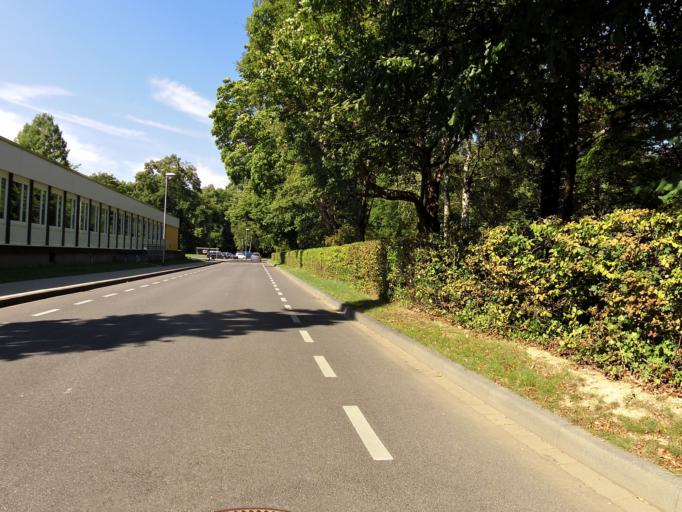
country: DE
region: North Rhine-Westphalia
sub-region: Regierungsbezirk Koln
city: Rheinbach
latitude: 50.6184
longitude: 6.9543
